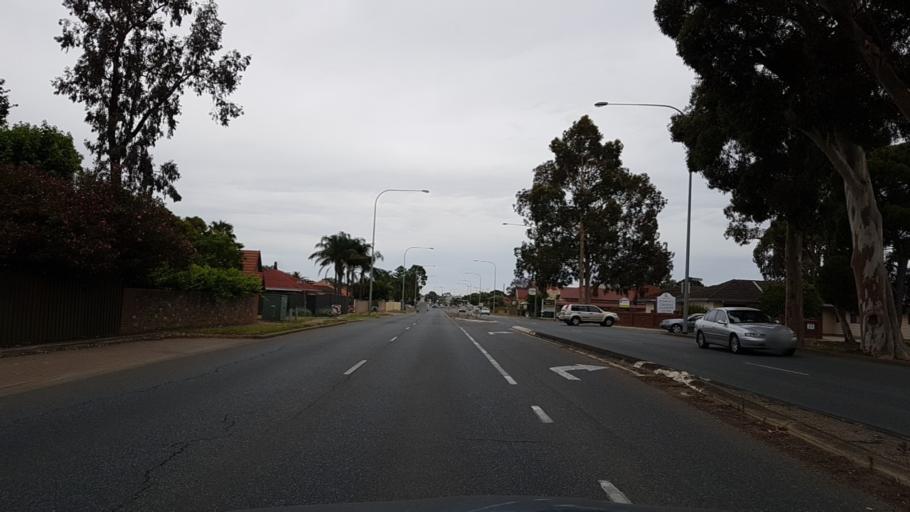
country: AU
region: South Australia
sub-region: Salisbury
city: Salisbury
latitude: -34.7571
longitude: 138.6459
